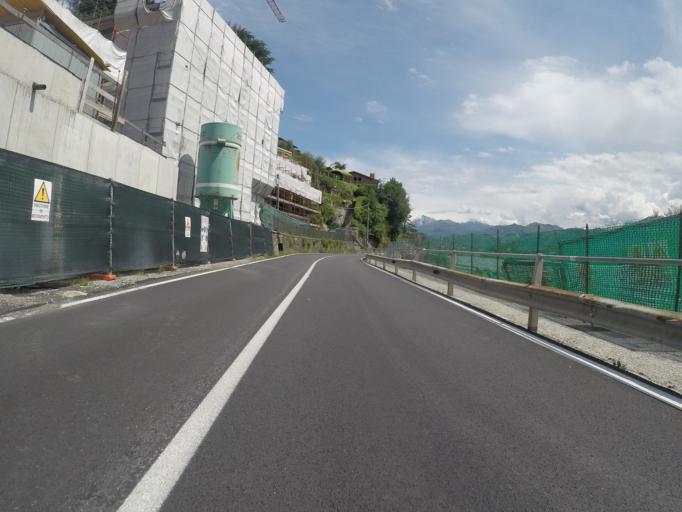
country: IT
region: Lombardy
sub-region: Provincia di Como
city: Colonno
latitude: 45.9595
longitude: 9.1600
